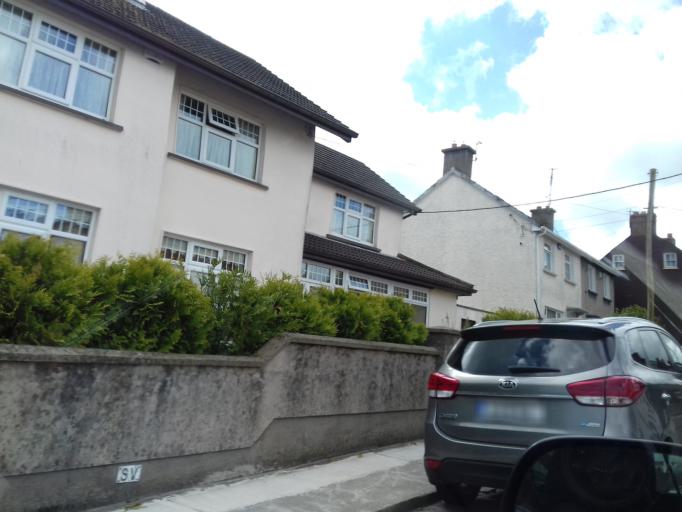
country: IE
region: Leinster
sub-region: Loch Garman
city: Loch Garman
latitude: 52.3325
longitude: -6.4535
